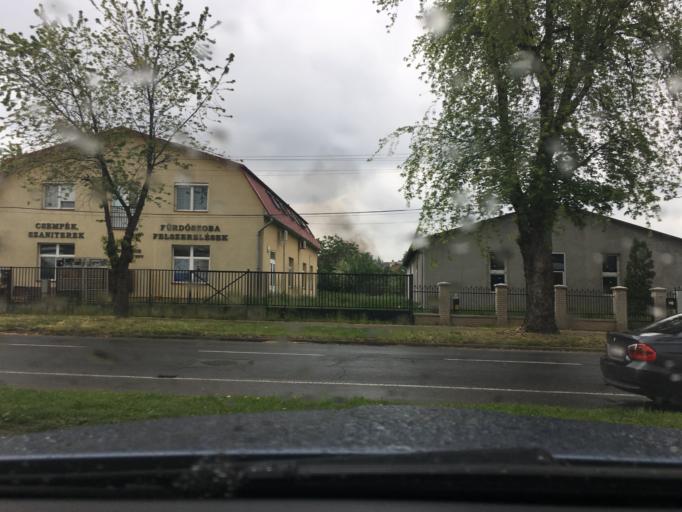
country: HU
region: Hajdu-Bihar
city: Debrecen
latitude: 47.5134
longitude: 21.6368
